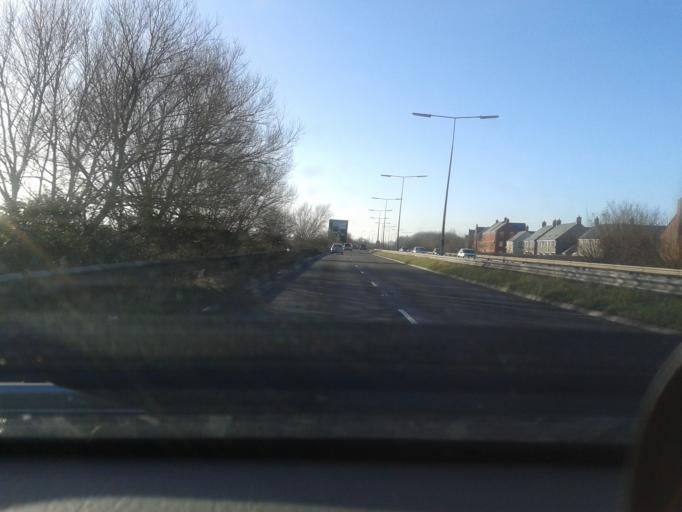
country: GB
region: England
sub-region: North Somerset
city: Hutton
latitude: 51.3460
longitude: -2.9250
